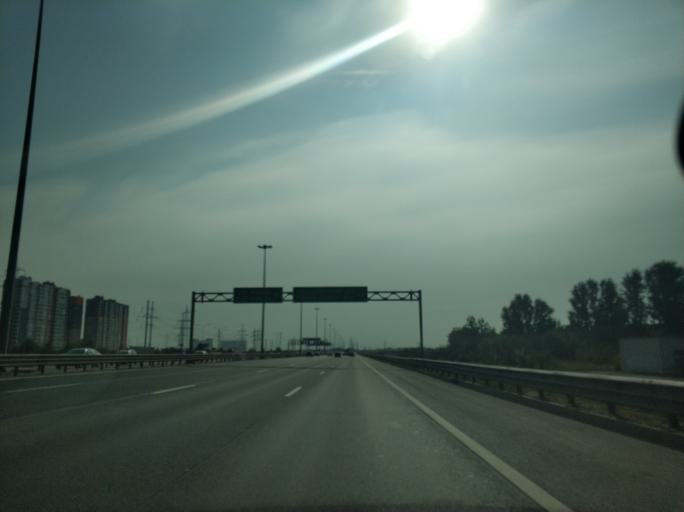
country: RU
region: Leningrad
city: Murino
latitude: 60.0292
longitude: 30.4460
